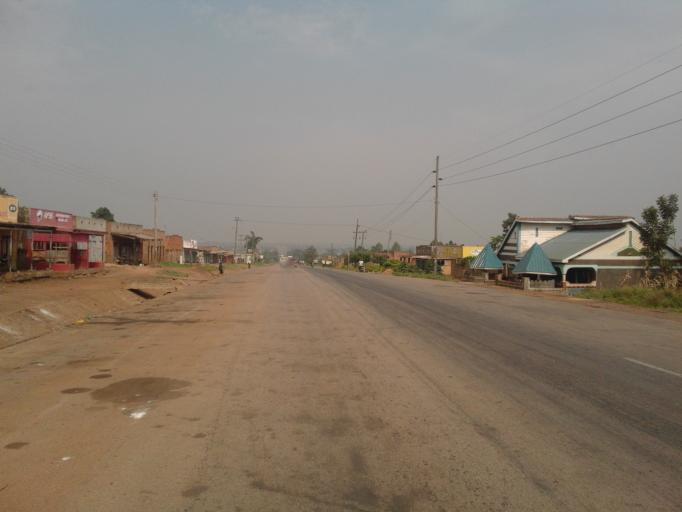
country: UG
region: Eastern Region
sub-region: Bugiri District
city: Bugiri
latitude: 0.5562
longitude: 33.7641
